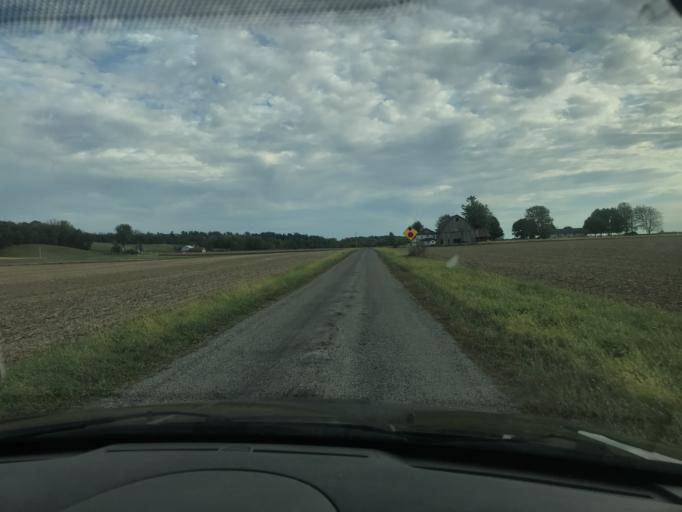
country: US
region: Ohio
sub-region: Logan County
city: West Liberty
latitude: 40.2362
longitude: -83.6854
